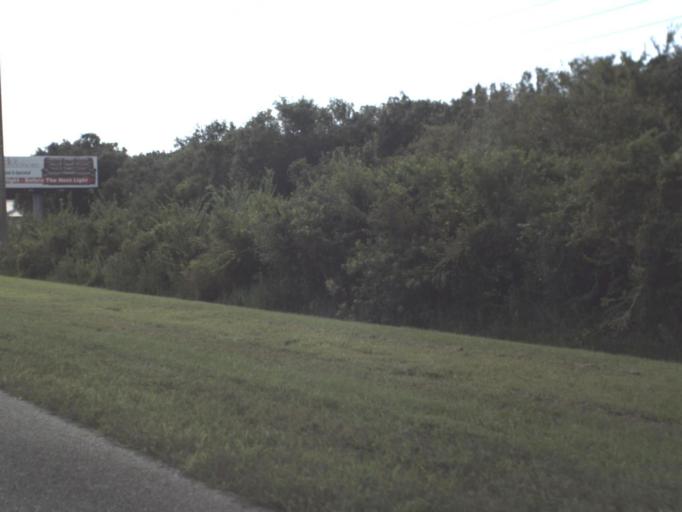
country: US
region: Florida
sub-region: Sarasota County
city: North Port
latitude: 27.0181
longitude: -82.1617
